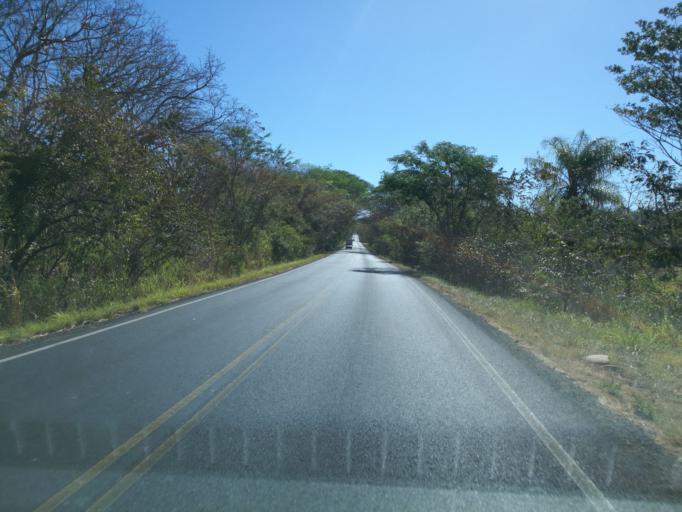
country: CR
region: Puntarenas
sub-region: Canton Central de Puntarenas
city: Puntarenas
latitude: 10.0885
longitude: -84.8503
